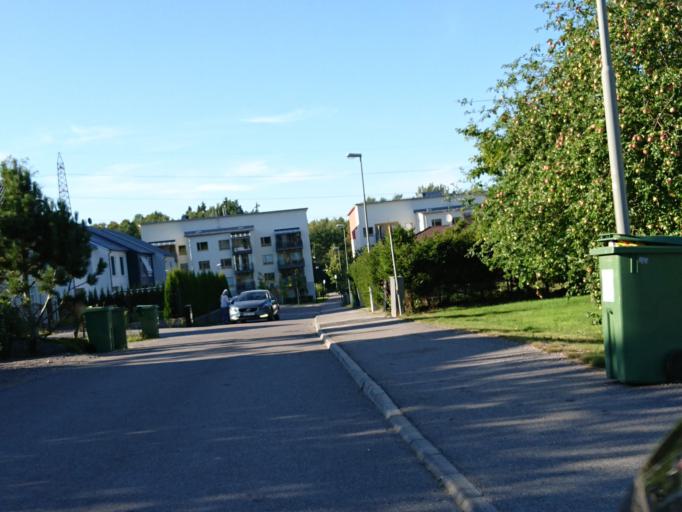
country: SE
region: Stockholm
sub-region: Huddinge Kommun
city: Segeltorp
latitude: 59.2798
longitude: 17.9287
